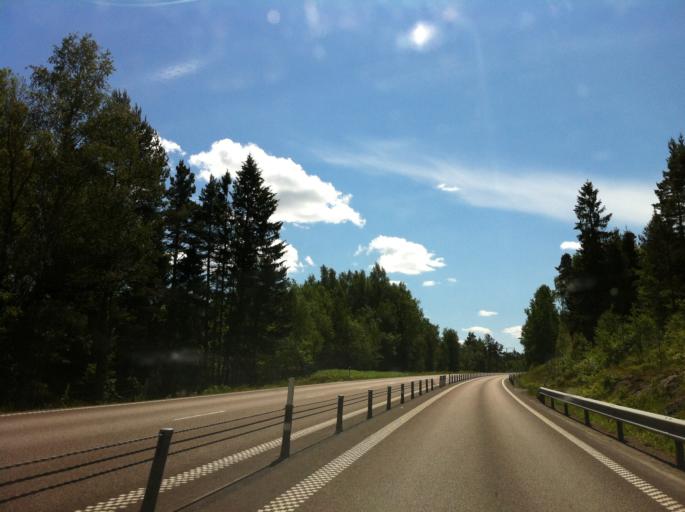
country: SE
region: Vaestra Goetaland
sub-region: Melleruds Kommun
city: Mellerud
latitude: 58.8129
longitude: 12.5238
